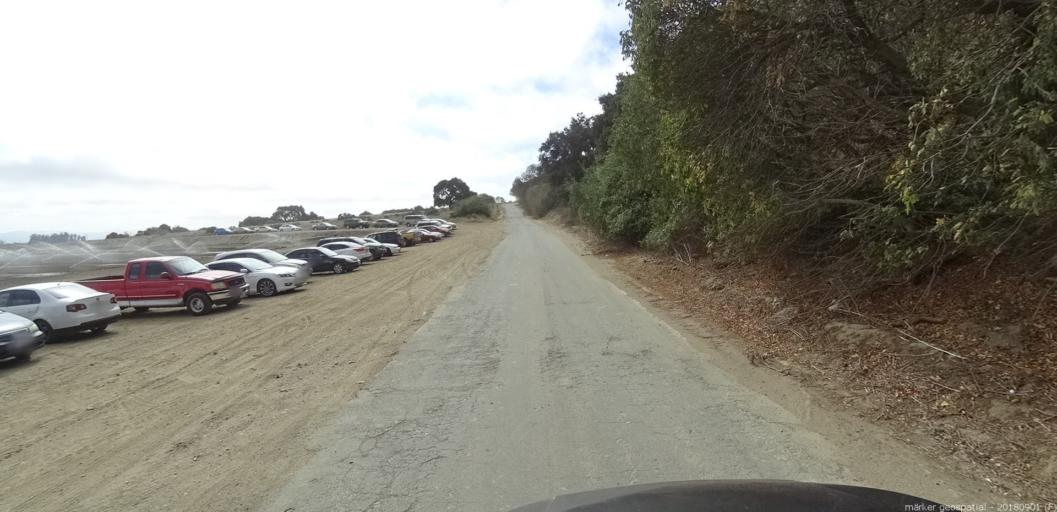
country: US
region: California
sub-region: Monterey County
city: Soledad
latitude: 36.4303
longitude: -121.4033
